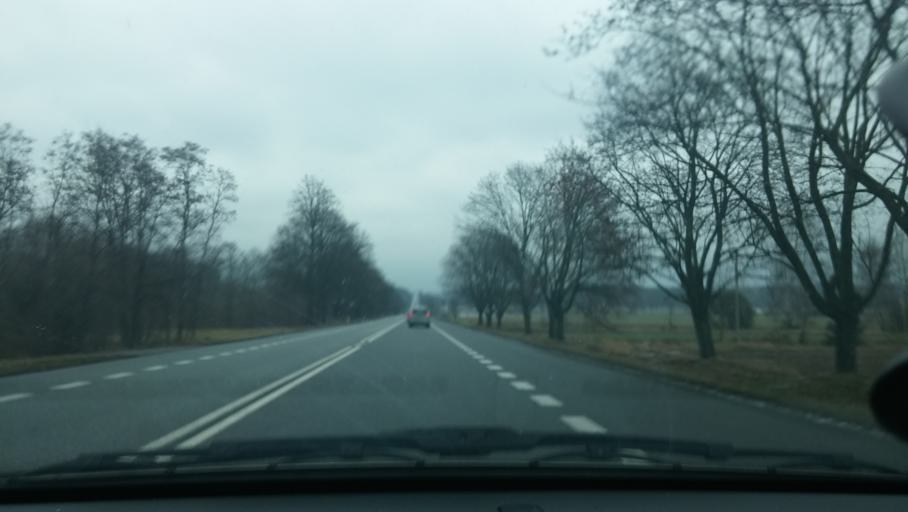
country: PL
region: Masovian Voivodeship
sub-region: Powiat wegrowski
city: Grebkow
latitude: 52.2027
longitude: 21.9657
